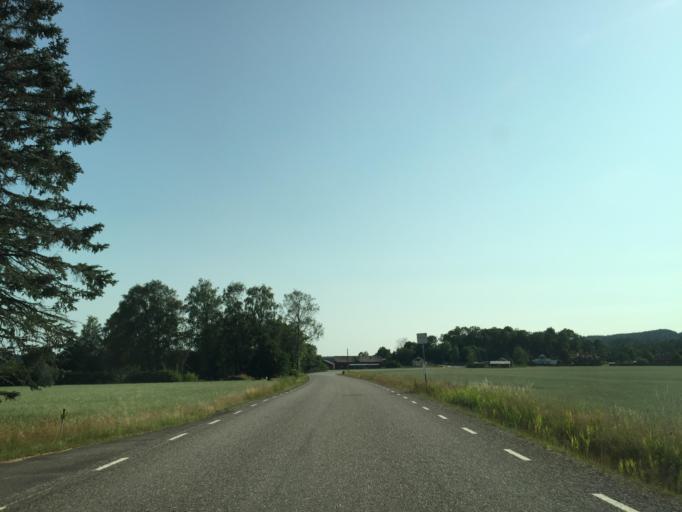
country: SE
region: Vaestra Goetaland
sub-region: Trollhattan
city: Sjuntorp
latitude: 58.2144
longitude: 12.1413
